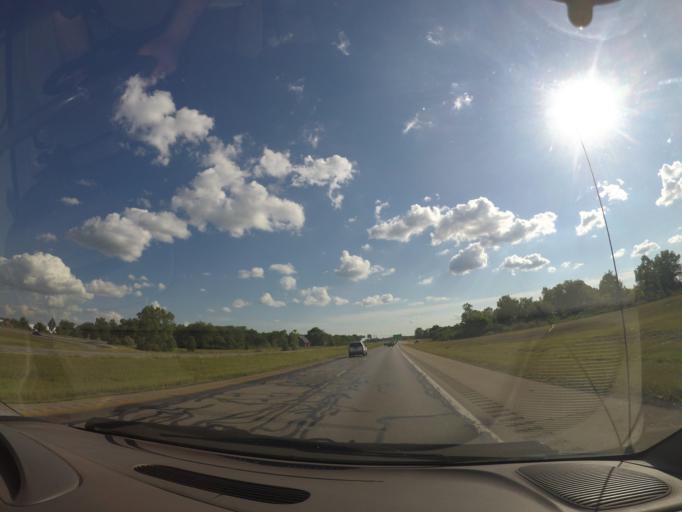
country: US
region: Ohio
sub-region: Lucas County
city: Waterville
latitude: 41.5403
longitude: -83.7043
